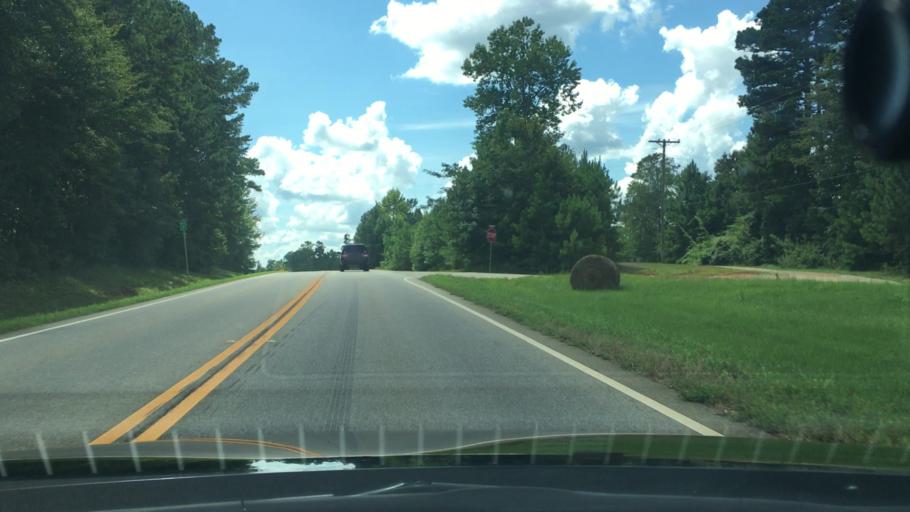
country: US
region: Georgia
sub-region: Putnam County
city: Eatonton
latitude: 33.3120
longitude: -83.4562
